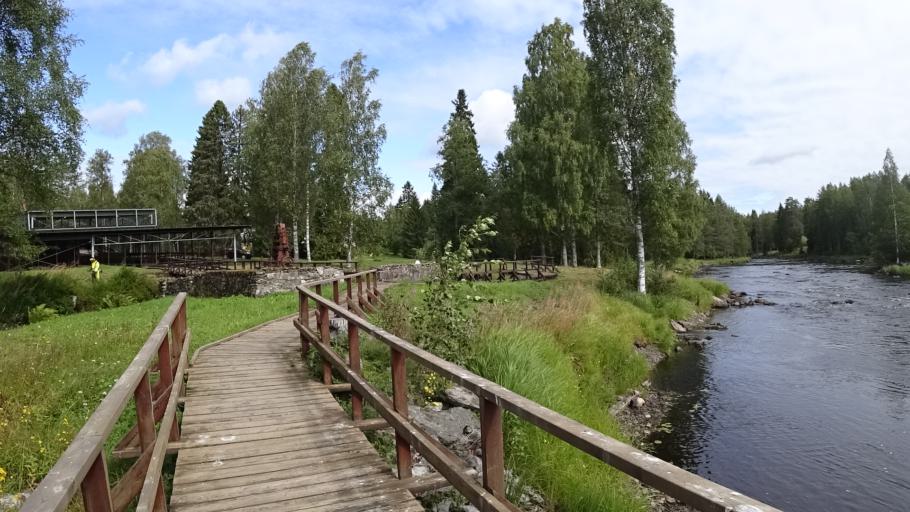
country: FI
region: North Karelia
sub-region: Joensuu
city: Ilomantsi
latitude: 62.6403
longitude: 31.2887
